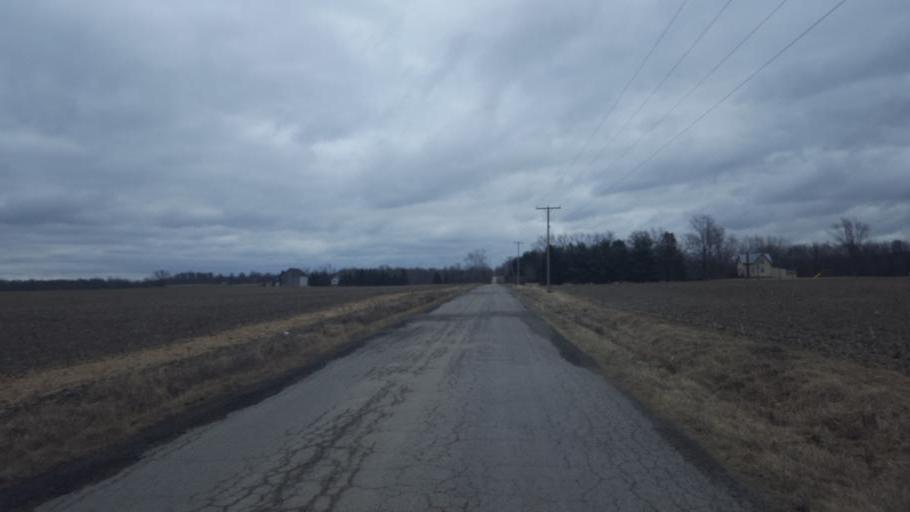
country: US
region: Ohio
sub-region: Morrow County
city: Mount Gilead
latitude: 40.6399
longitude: -82.8576
